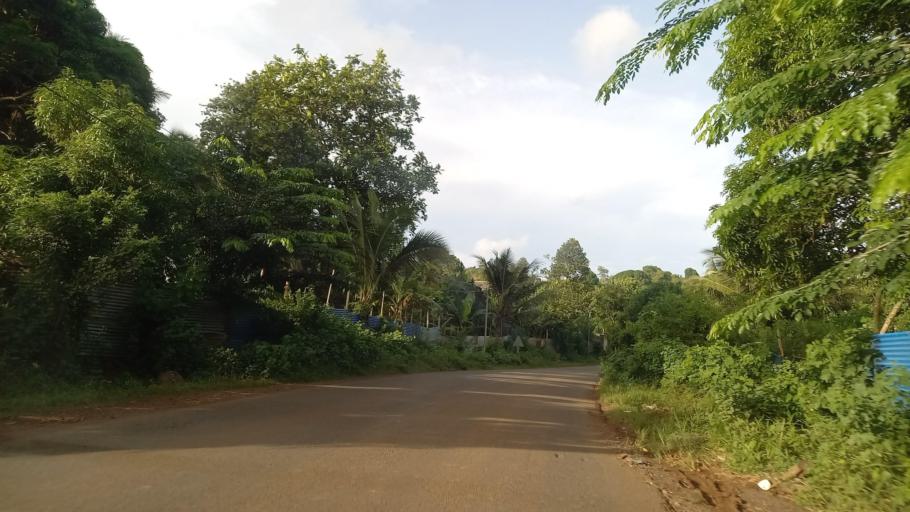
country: YT
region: Bandraboua
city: Bandraboua
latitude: -12.7286
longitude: 45.1201
